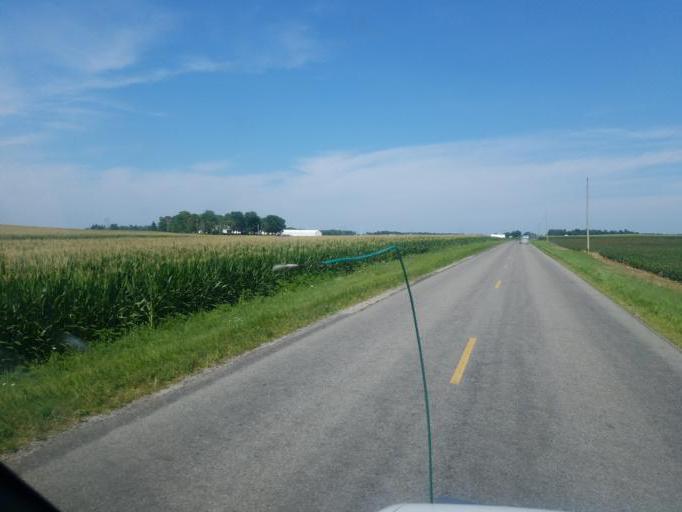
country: US
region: Ohio
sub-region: Shelby County
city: Botkins
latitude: 40.4977
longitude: -84.1111
